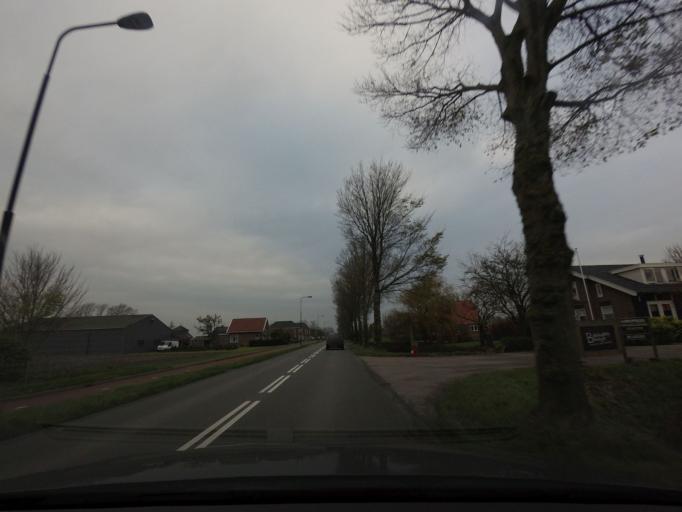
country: NL
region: North Holland
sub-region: Gemeente Heerhugowaard
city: Heerhugowaard
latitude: 52.6926
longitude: 4.8506
